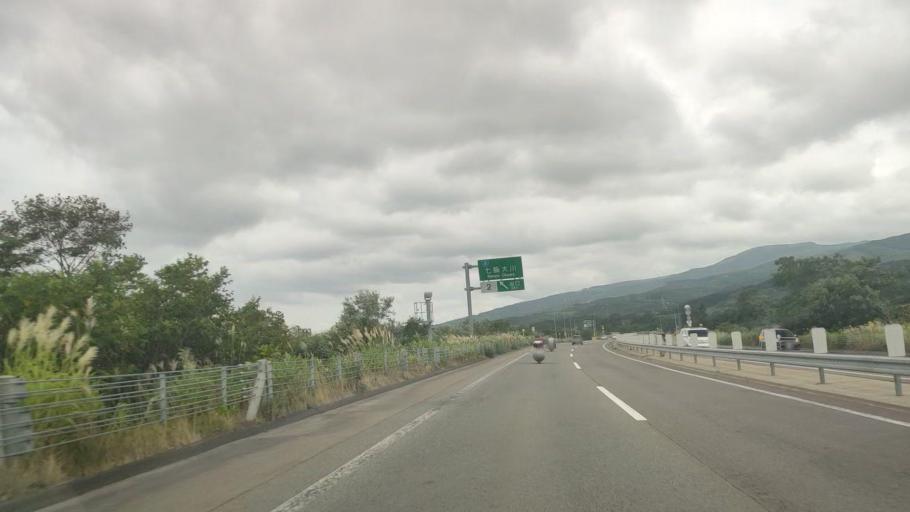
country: JP
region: Hokkaido
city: Nanae
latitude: 41.8641
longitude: 140.7308
